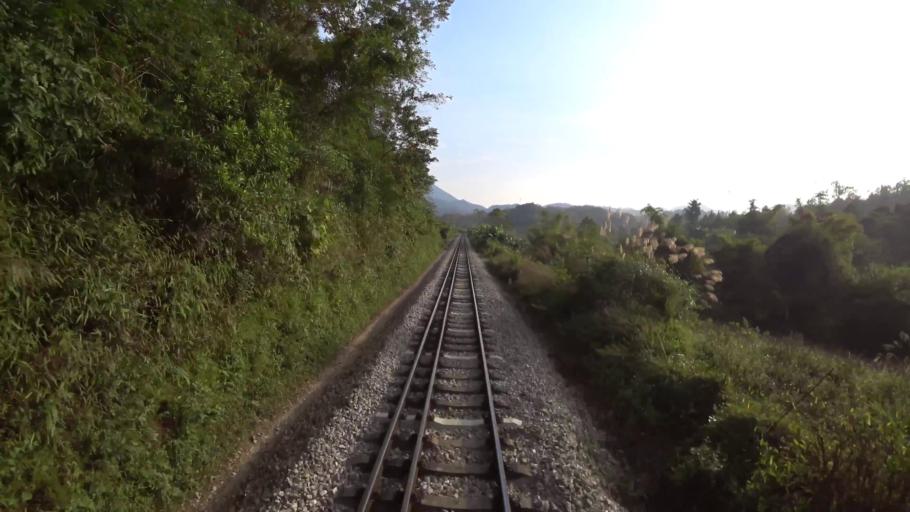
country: VN
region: Lang Son
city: Thi Tran Cao Loc
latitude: 21.9230
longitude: 106.7066
